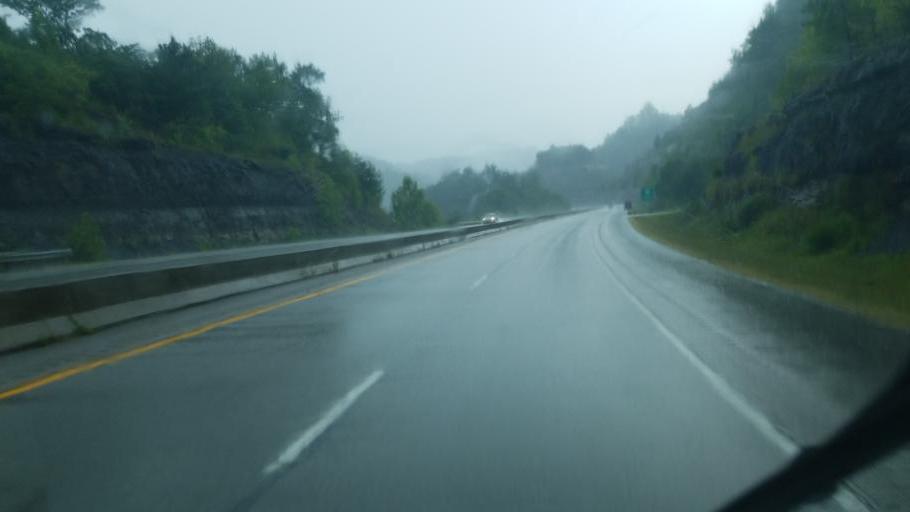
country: US
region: West Virginia
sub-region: Mingo County
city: Williamson
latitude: 37.6146
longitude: -82.3418
